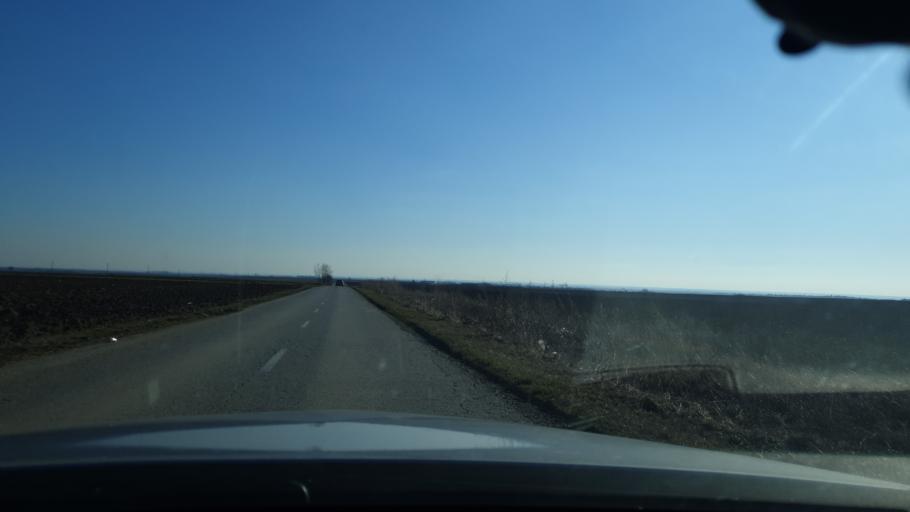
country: RS
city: Vrdnik
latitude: 45.0822
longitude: 19.8075
